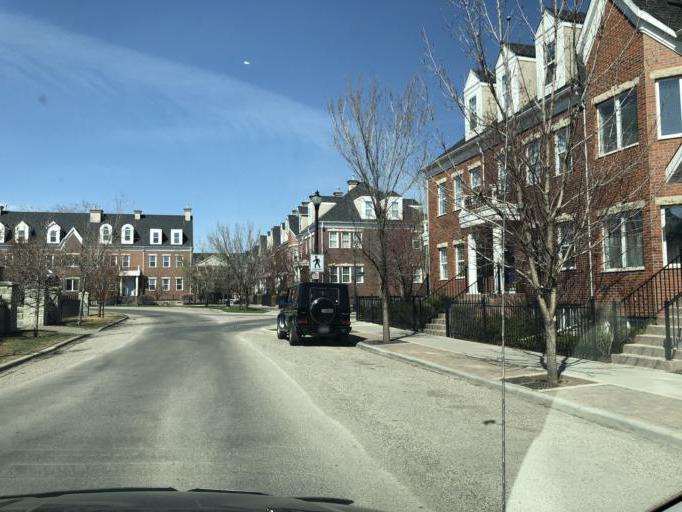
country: CA
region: Alberta
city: Calgary
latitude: 51.0211
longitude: -114.1136
